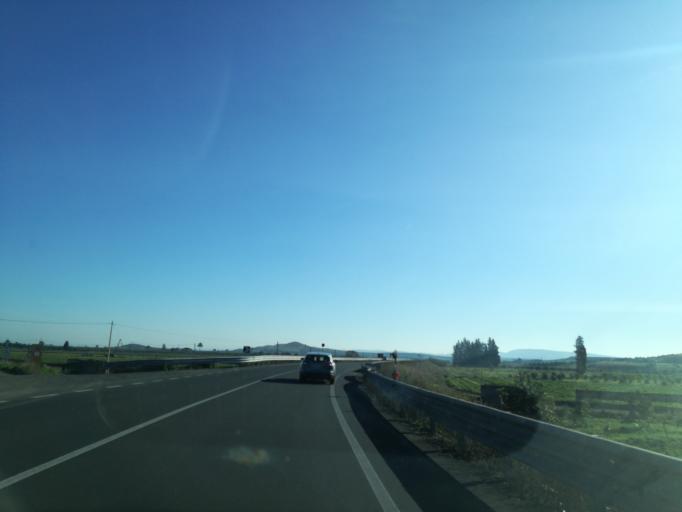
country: IT
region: Sicily
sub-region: Catania
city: Palagonia
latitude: 37.3810
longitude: 14.7707
